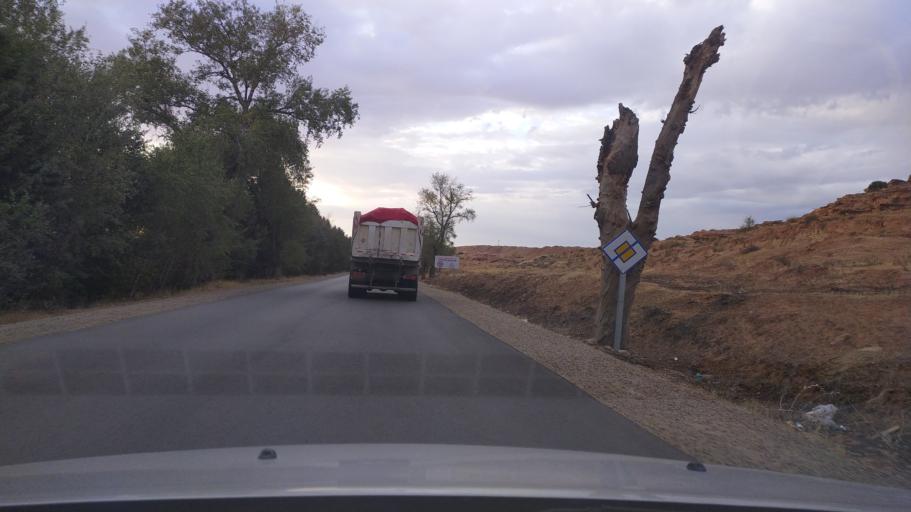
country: DZ
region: Tiaret
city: Frenda
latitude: 35.0493
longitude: 1.0780
